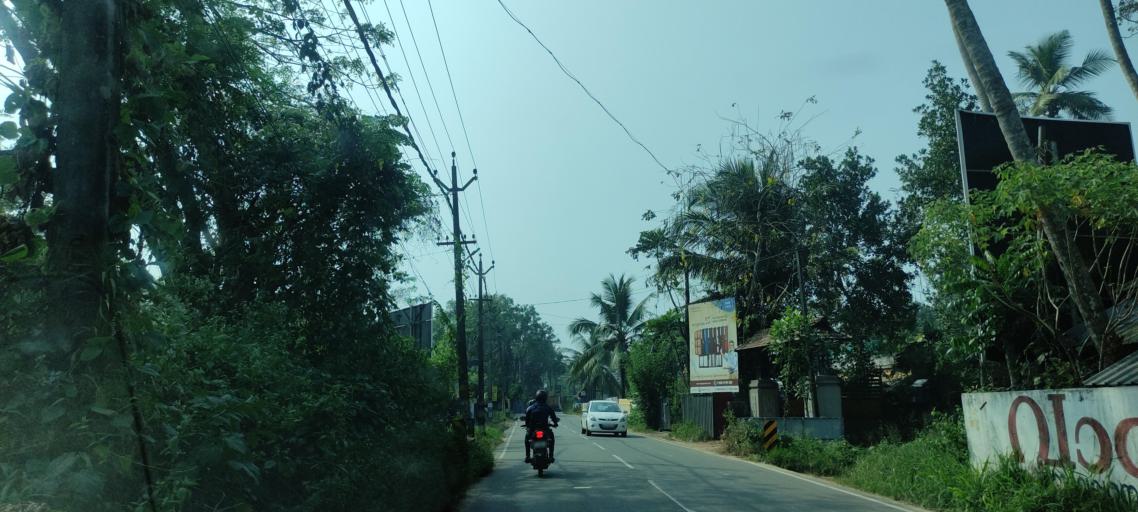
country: IN
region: Kerala
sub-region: Alappuzha
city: Vayalar
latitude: 9.6965
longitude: 76.3221
